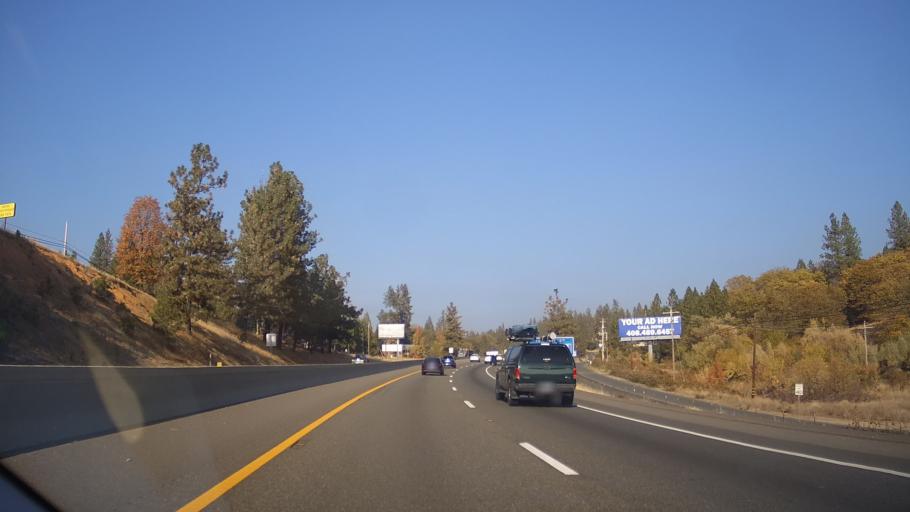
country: US
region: California
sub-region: Placer County
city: Colfax
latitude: 39.0864
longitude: -120.9557
